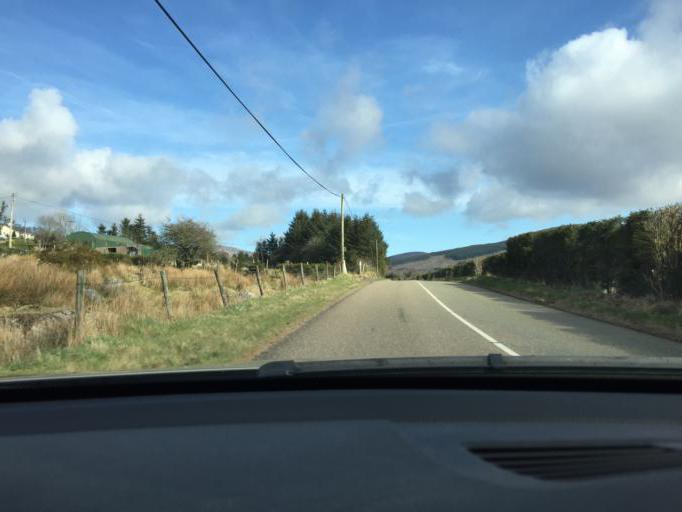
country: IE
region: Leinster
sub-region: Wicklow
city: Valleymount
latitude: 53.0608
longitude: -6.4844
